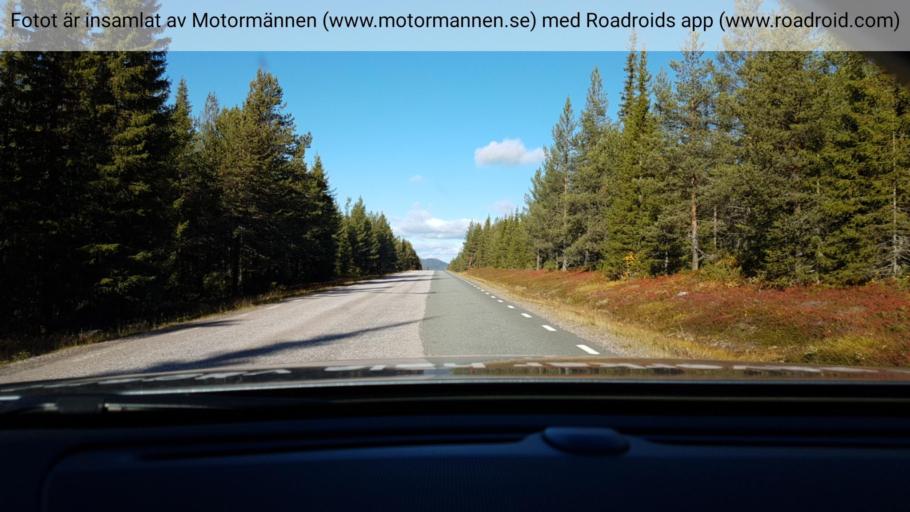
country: SE
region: Norrbotten
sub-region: Arjeplogs Kommun
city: Arjeplog
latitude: 65.8097
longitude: 18.4582
